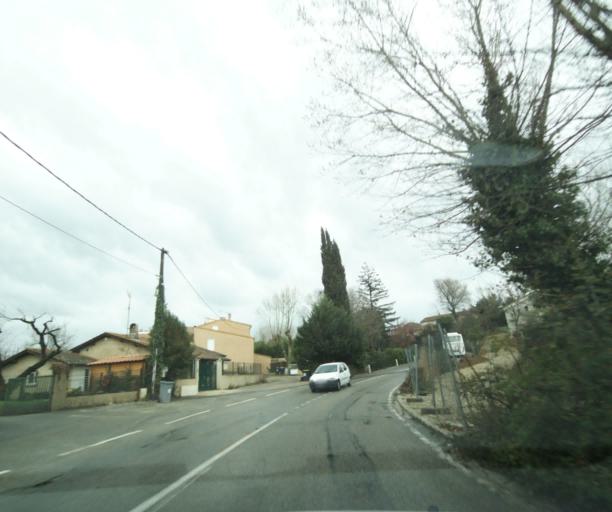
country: FR
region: Rhone-Alpes
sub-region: Departement de la Drome
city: Bourg-les-Valence
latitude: 44.9626
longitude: 4.8978
